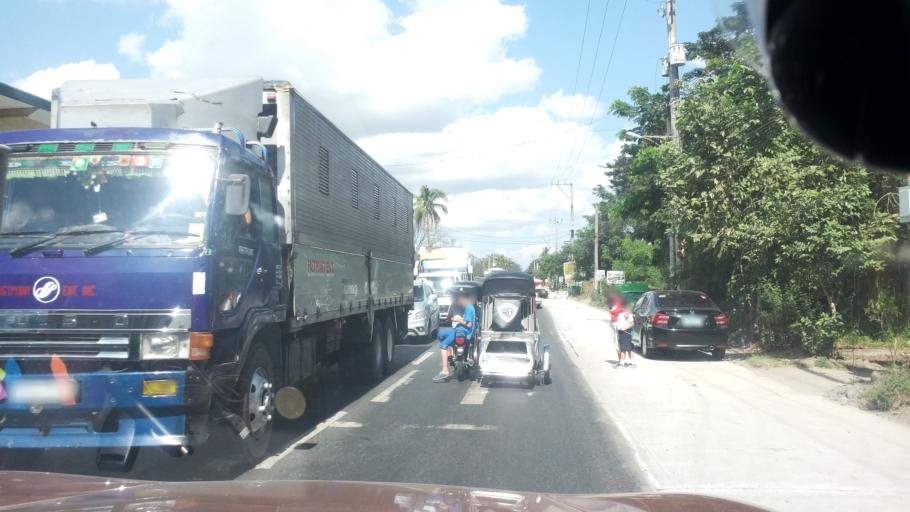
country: PH
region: Central Luzon
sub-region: Province of Bulacan
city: Plaridel
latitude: 14.8744
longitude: 120.8624
